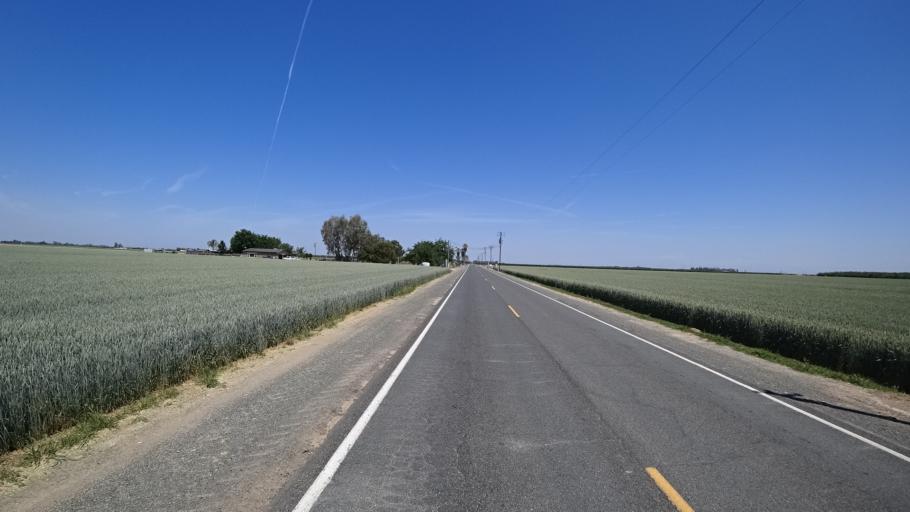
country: US
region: California
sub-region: Kings County
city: Armona
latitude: 36.2294
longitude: -119.7088
